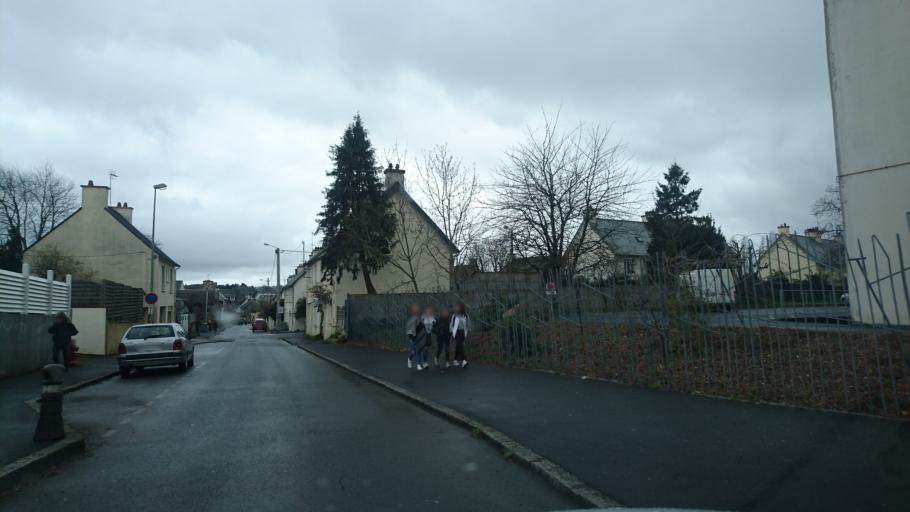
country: FR
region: Brittany
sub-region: Departement des Cotes-d'Armor
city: Lannion
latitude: 48.7306
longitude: -3.4486
